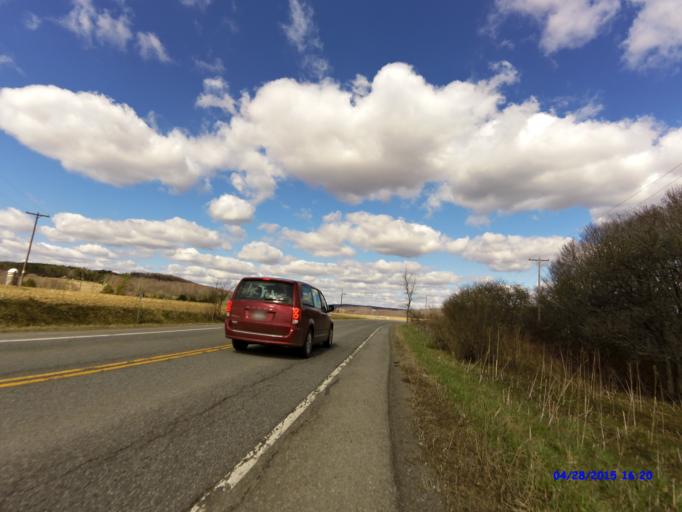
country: US
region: New York
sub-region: Cattaraugus County
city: Franklinville
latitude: 42.3737
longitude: -78.4462
